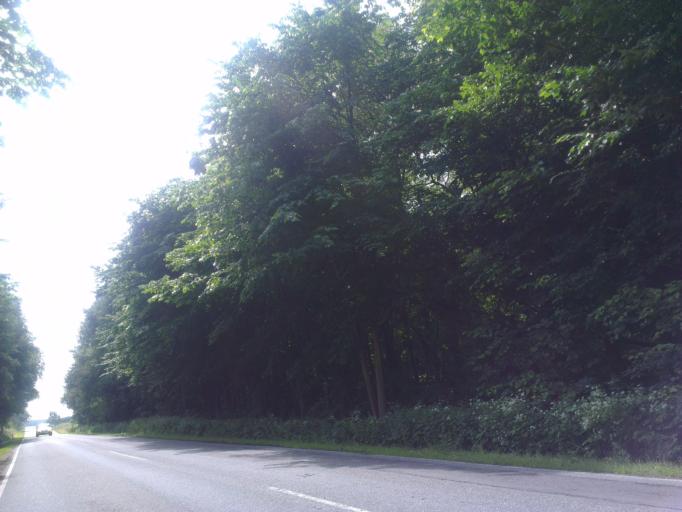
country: DK
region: Capital Region
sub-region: Frederikssund Kommune
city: Jaegerspris
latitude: 55.8726
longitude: 11.9592
